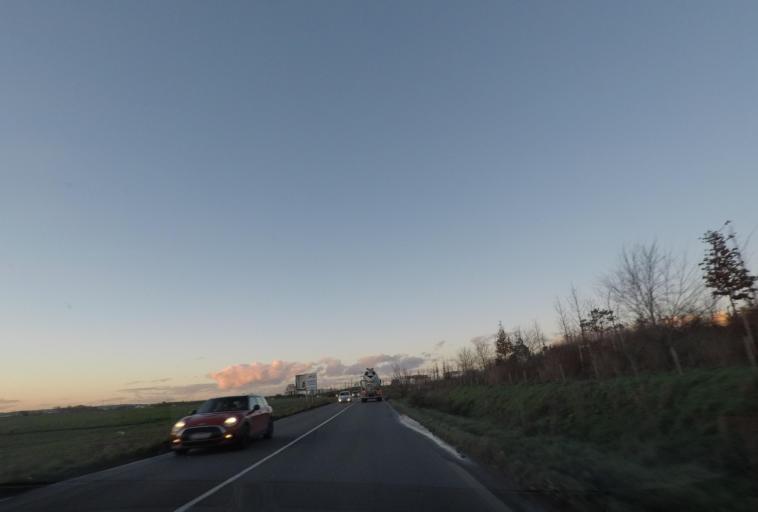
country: FR
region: Ile-de-France
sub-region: Departement de l'Essonne
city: Le Plessis-Pate
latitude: 48.6141
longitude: 2.3461
